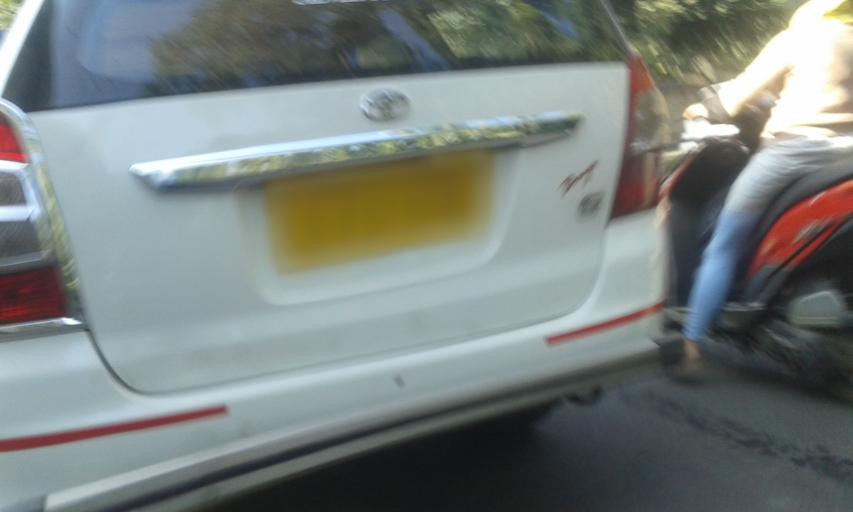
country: IN
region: Karnataka
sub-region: Bangalore Urban
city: Bangalore
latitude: 12.9301
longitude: 77.6227
